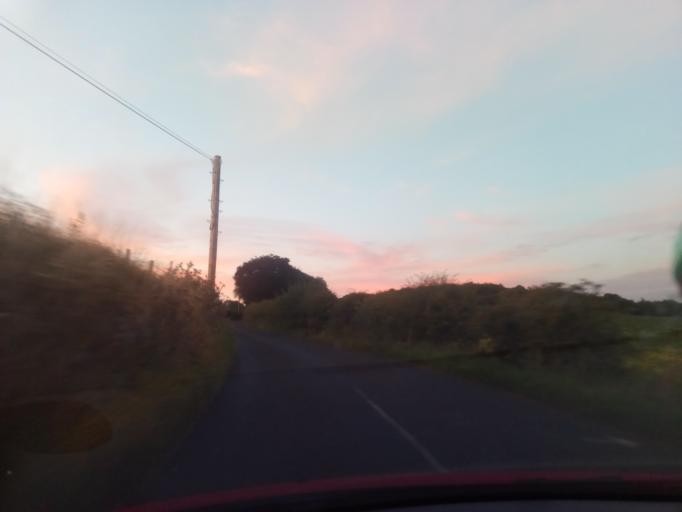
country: GB
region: England
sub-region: Northumberland
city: Warden
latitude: 54.9832
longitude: -2.2259
